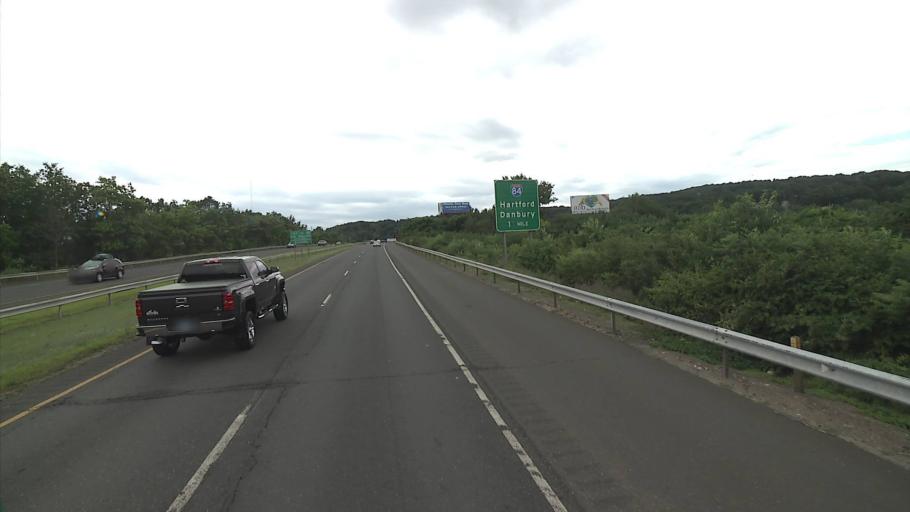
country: US
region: Connecticut
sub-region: New Haven County
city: Waterbury
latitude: 41.5716
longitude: -73.0553
